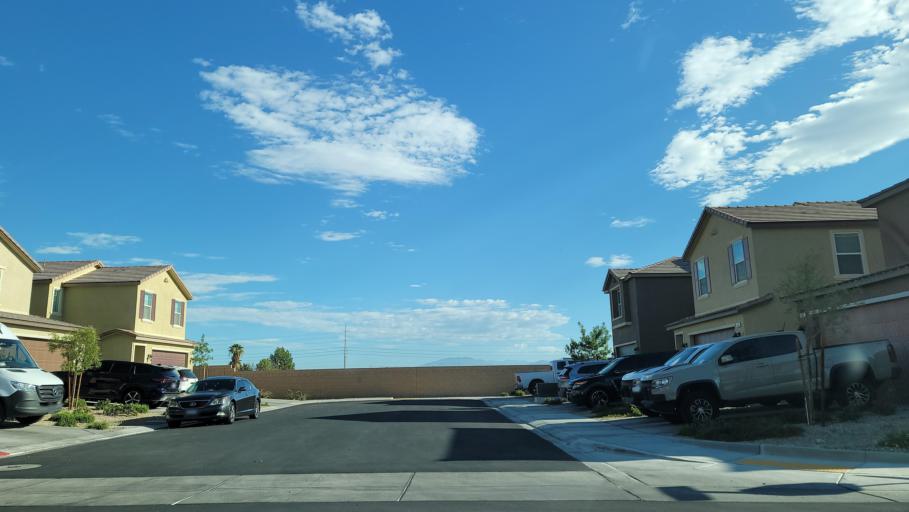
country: US
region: Nevada
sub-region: Clark County
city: Spring Valley
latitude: 36.0827
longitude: -115.2616
